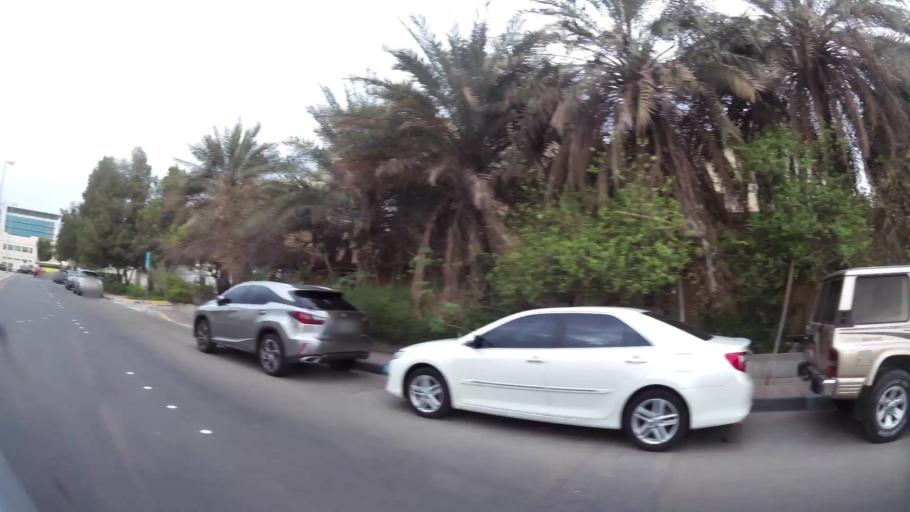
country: AE
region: Abu Dhabi
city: Abu Dhabi
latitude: 24.4819
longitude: 54.3822
